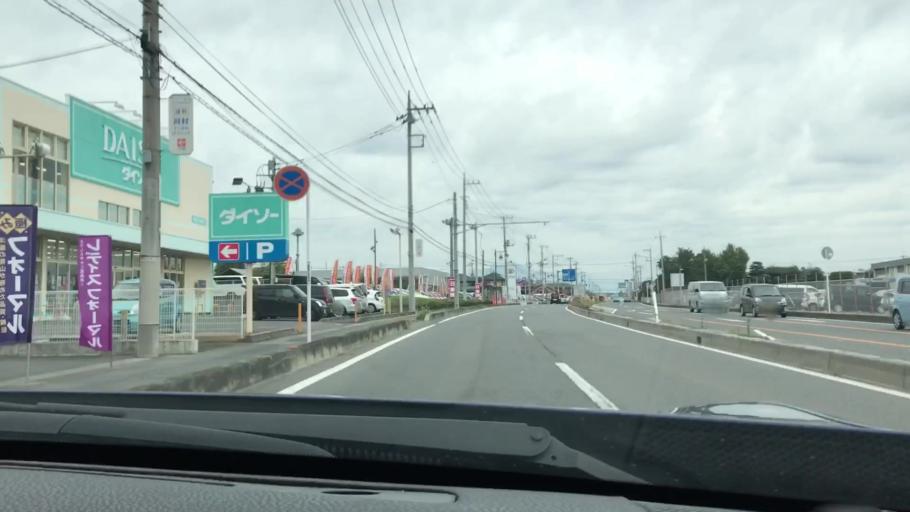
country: JP
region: Gunma
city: Kanekomachi
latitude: 36.3926
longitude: 139.0078
